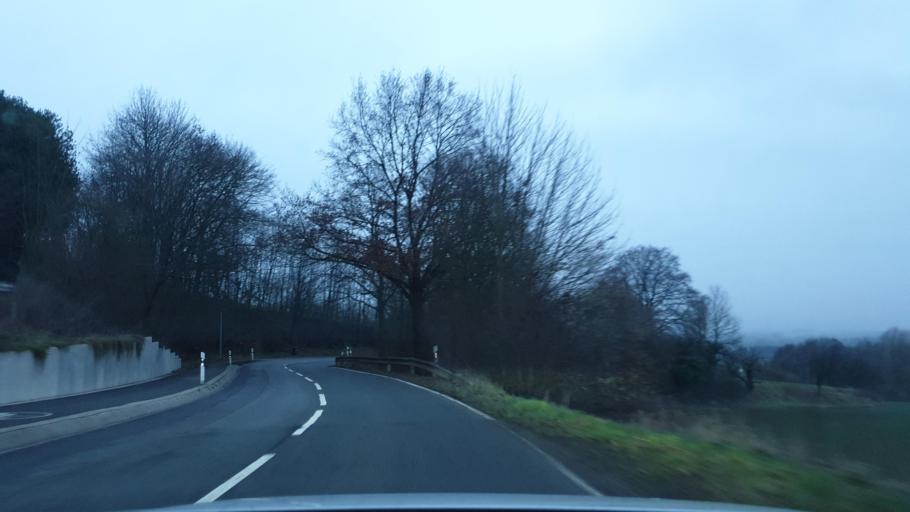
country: DE
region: North Rhine-Westphalia
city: Bad Oeynhausen
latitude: 52.2649
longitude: 8.7761
